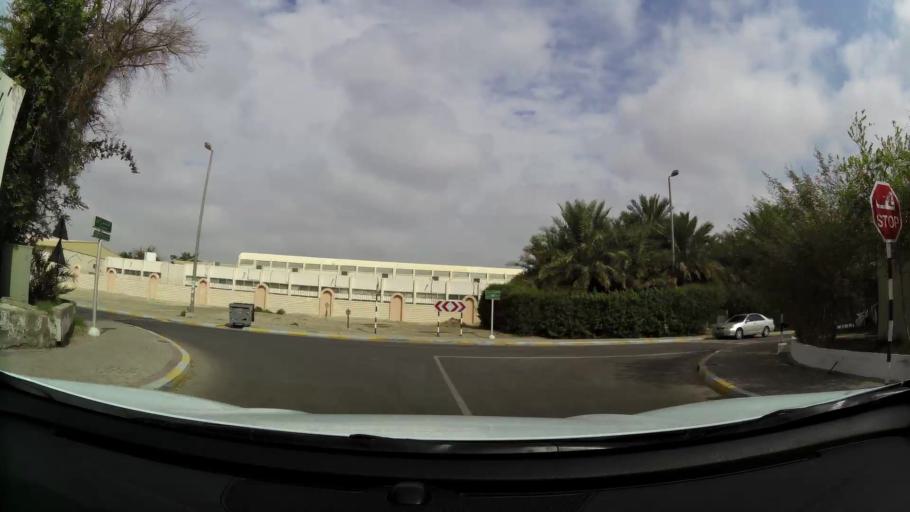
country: AE
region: Abu Dhabi
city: Al Ain
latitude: 24.2289
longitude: 55.7544
